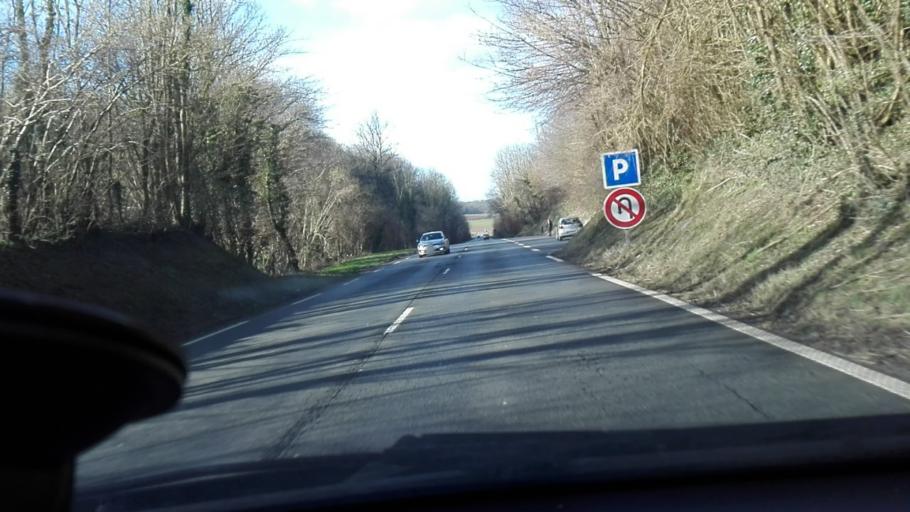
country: FR
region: Nord-Pas-de-Calais
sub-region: Departement du Pas-de-Calais
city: Licques
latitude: 50.7149
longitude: 1.9610
